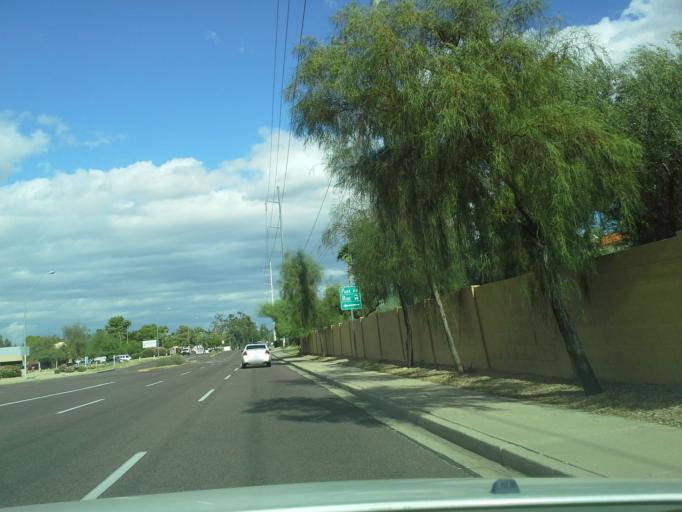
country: US
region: Arizona
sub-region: Maricopa County
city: Glendale
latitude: 33.6091
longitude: -112.0651
